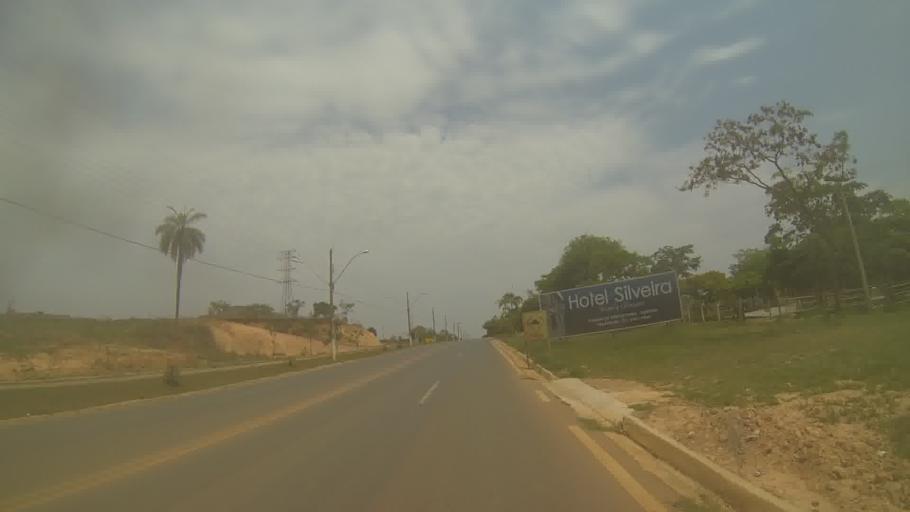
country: BR
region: Minas Gerais
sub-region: Bambui
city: Bambui
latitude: -20.0149
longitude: -45.9576
